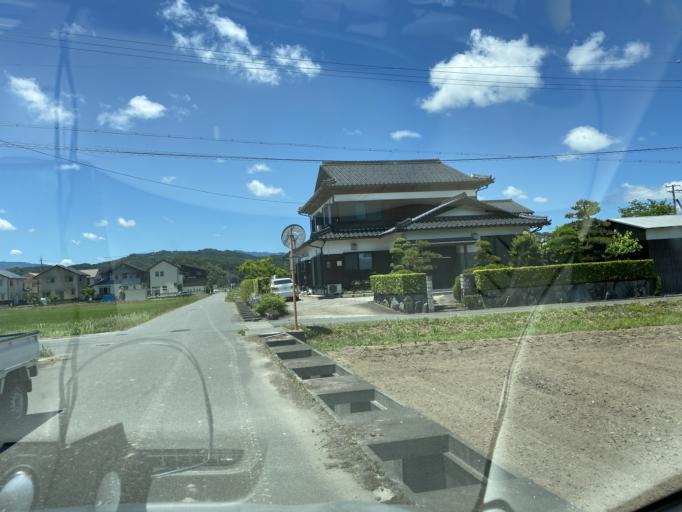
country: JP
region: Hyogo
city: Toyooka
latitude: 35.4842
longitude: 134.7928
